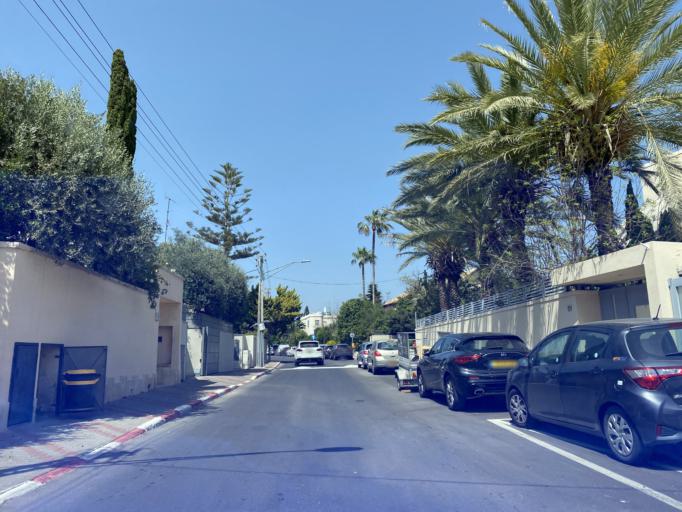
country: IL
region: Tel Aviv
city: Herzliya Pituah
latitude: 32.1718
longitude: 34.8104
